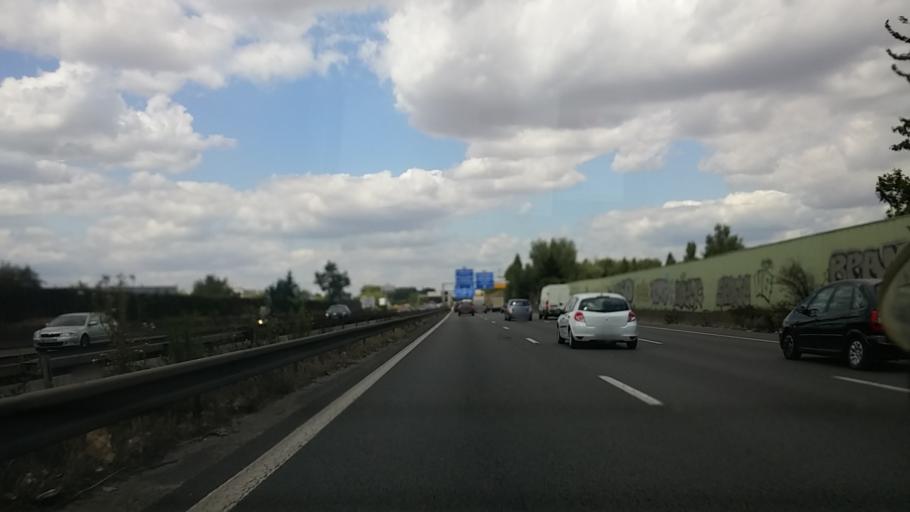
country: FR
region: Ile-de-France
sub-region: Departement de Seine-Saint-Denis
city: Aulnay-sous-Bois
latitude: 48.9409
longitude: 2.4788
